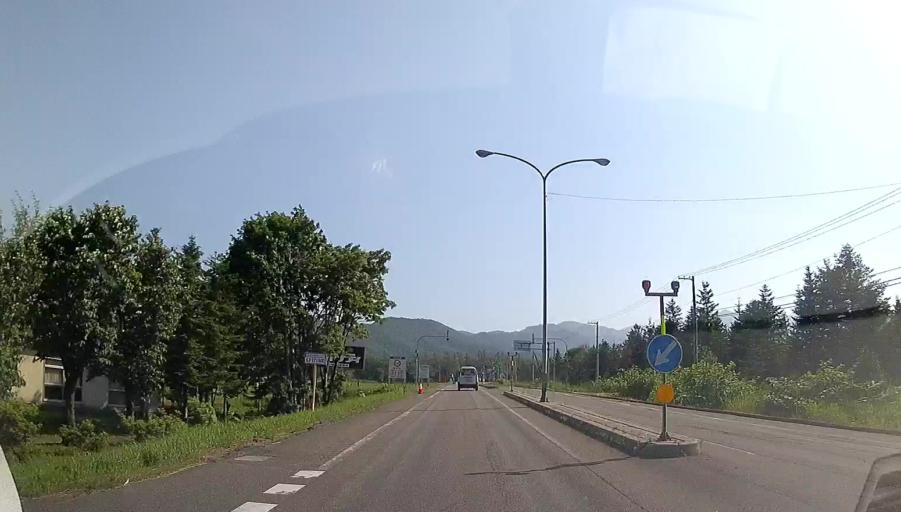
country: JP
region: Hokkaido
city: Otofuke
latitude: 42.9860
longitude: 142.8388
